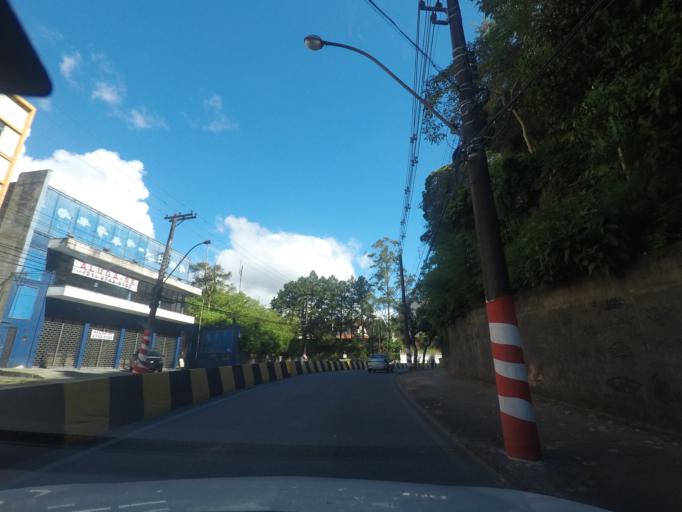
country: BR
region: Rio de Janeiro
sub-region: Teresopolis
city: Teresopolis
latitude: -22.4279
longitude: -42.9808
